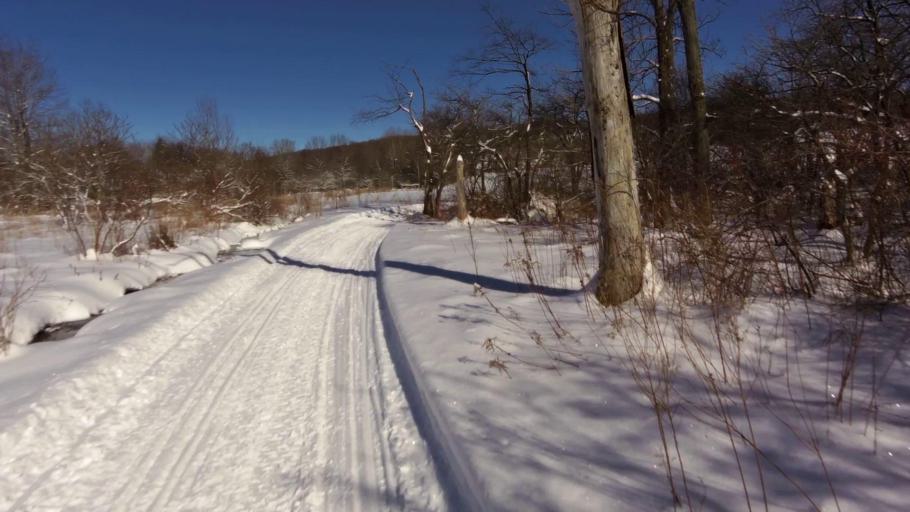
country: US
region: New York
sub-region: Chautauqua County
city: Silver Creek
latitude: 42.3737
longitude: -79.1525
